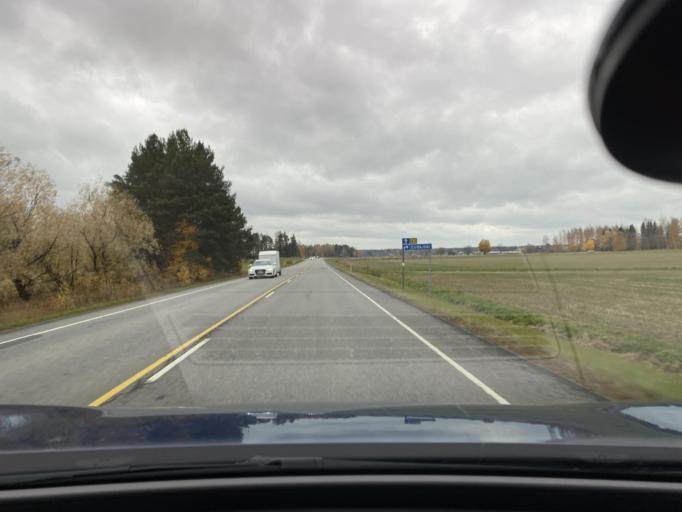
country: FI
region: Satakunta
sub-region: Rauma
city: Kiukainen
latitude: 61.1890
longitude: 22.0604
